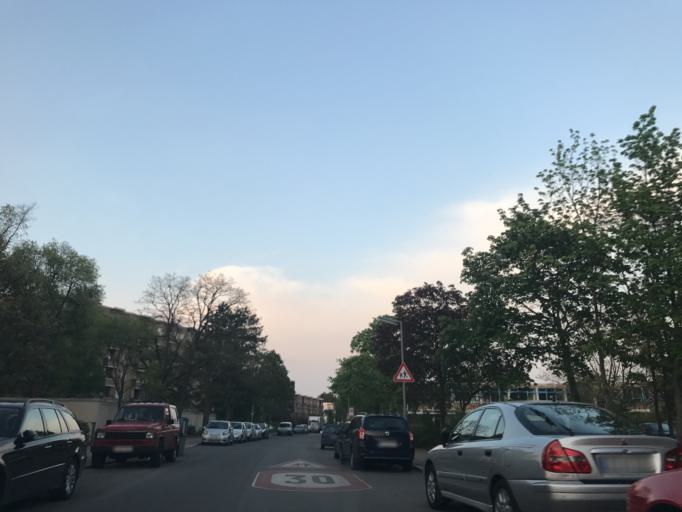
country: DE
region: Berlin
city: Staaken
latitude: 52.5310
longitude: 13.1553
